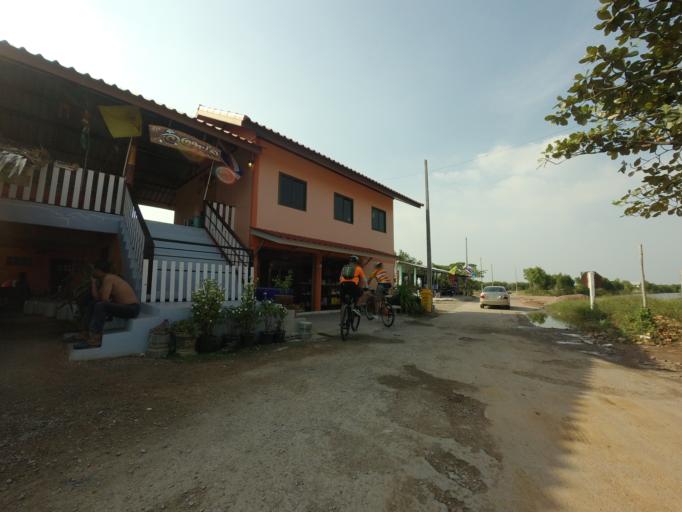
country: TH
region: Samut Sakhon
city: Samut Sakhon
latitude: 13.4883
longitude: 100.3620
